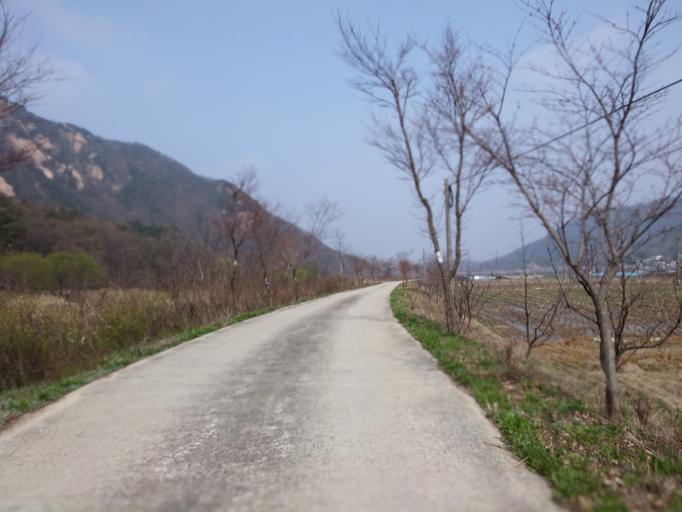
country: KR
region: Daejeon
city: Songgang-dong
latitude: 36.3736
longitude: 127.2582
